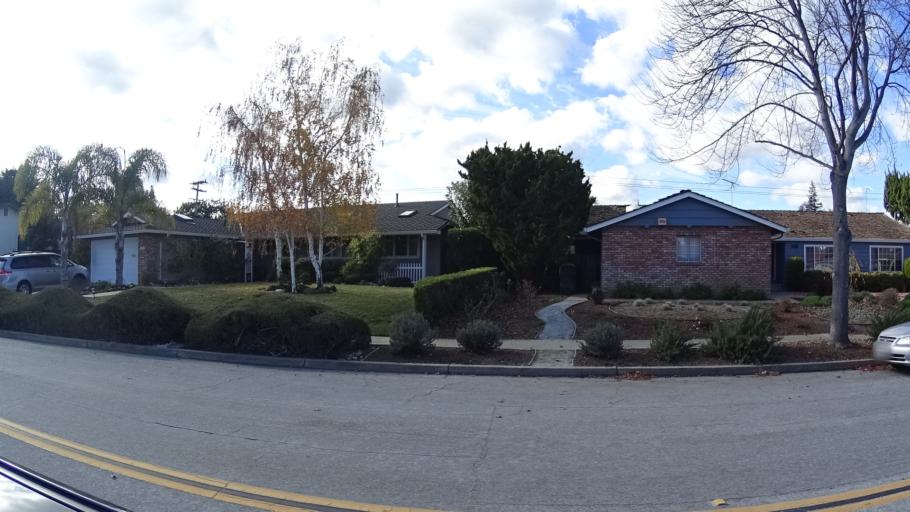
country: US
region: California
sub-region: Santa Clara County
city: Sunnyvale
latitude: 37.3456
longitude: -122.0454
